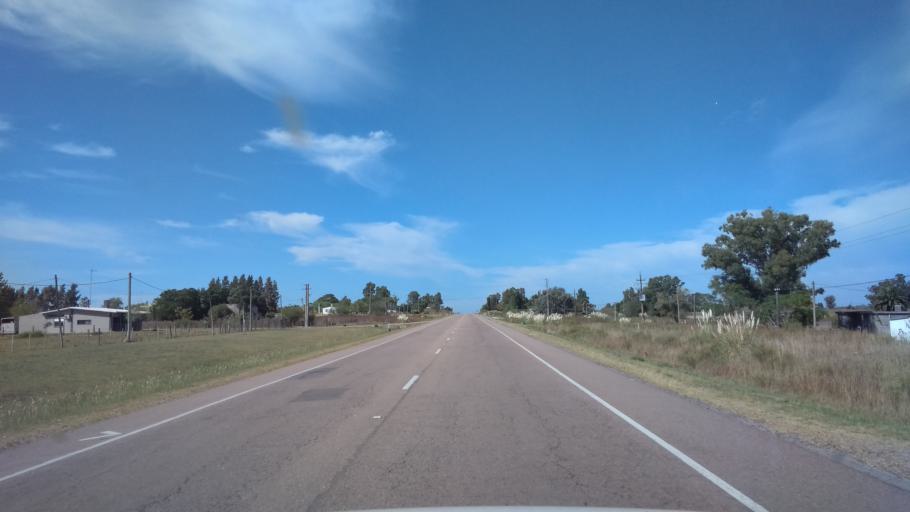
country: UY
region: Canelones
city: Sauce
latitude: -34.6185
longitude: -56.0497
